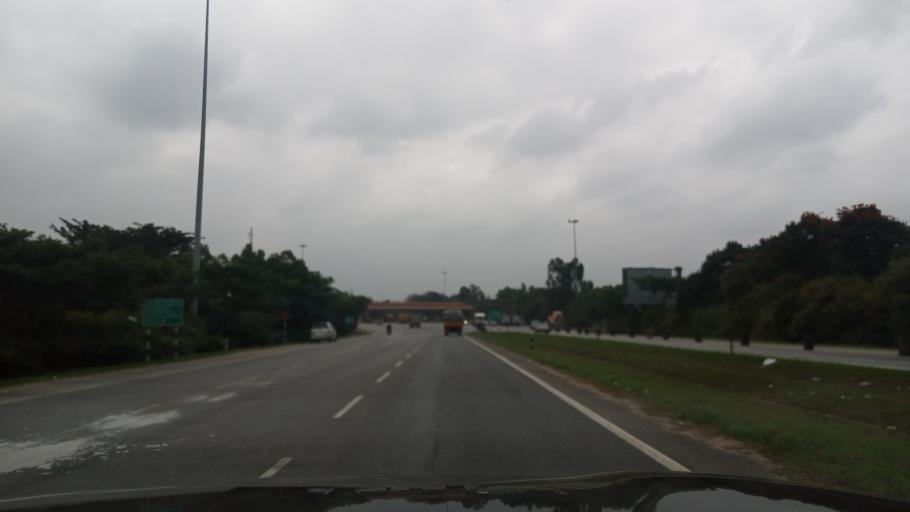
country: IN
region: Karnataka
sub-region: Bangalore Rural
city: Nelamangala
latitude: 13.0455
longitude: 77.4755
